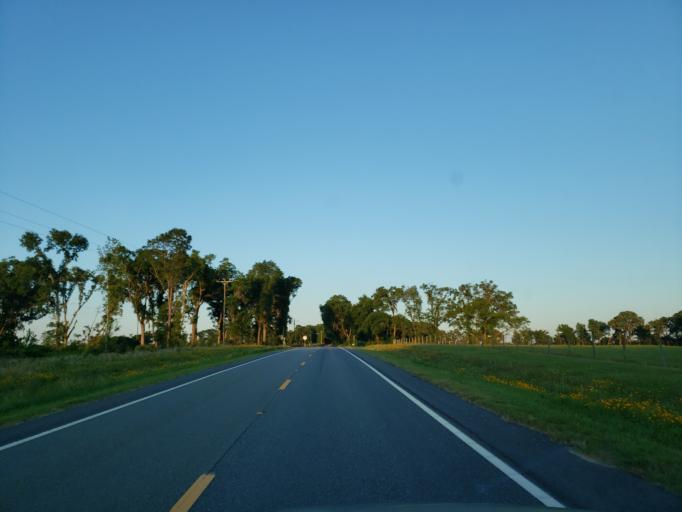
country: US
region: Florida
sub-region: Madison County
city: Madison
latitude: 30.5977
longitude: -83.2513
